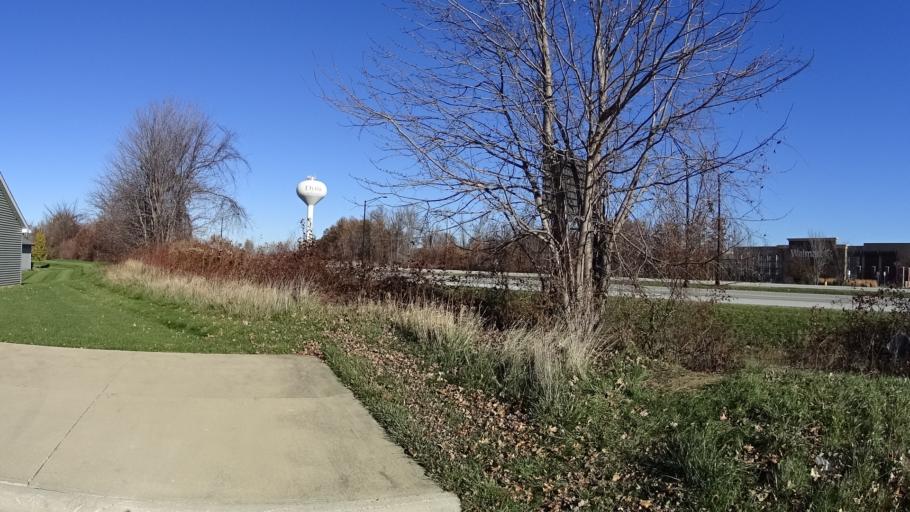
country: US
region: Ohio
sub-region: Lorain County
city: Elyria
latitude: 41.3500
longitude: -82.0699
